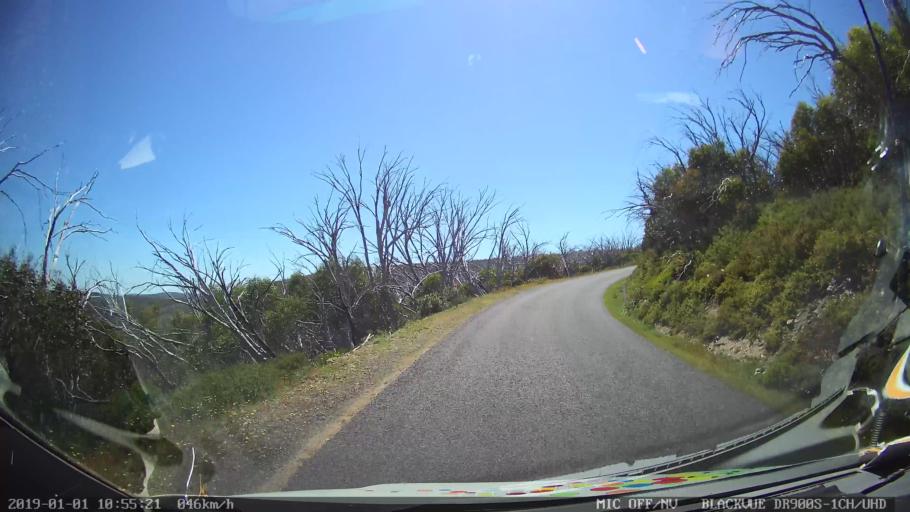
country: AU
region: New South Wales
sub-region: Snowy River
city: Jindabyne
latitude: -36.0083
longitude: 148.3879
